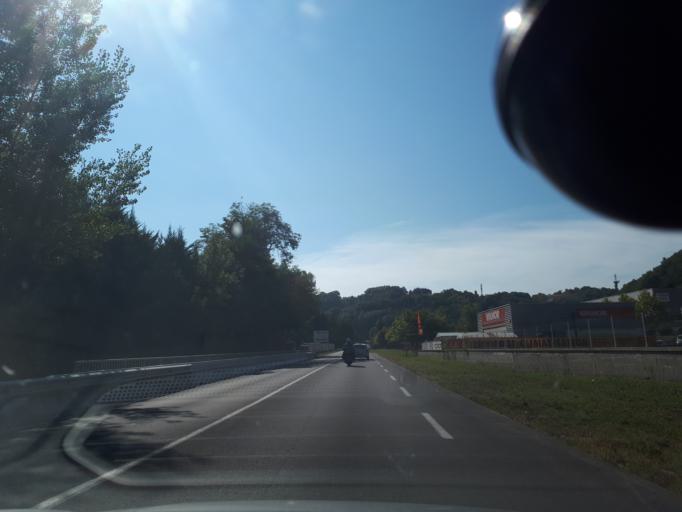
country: FR
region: Rhone-Alpes
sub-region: Departement de l'Isere
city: Bourgoin
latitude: 45.5710
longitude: 5.2793
